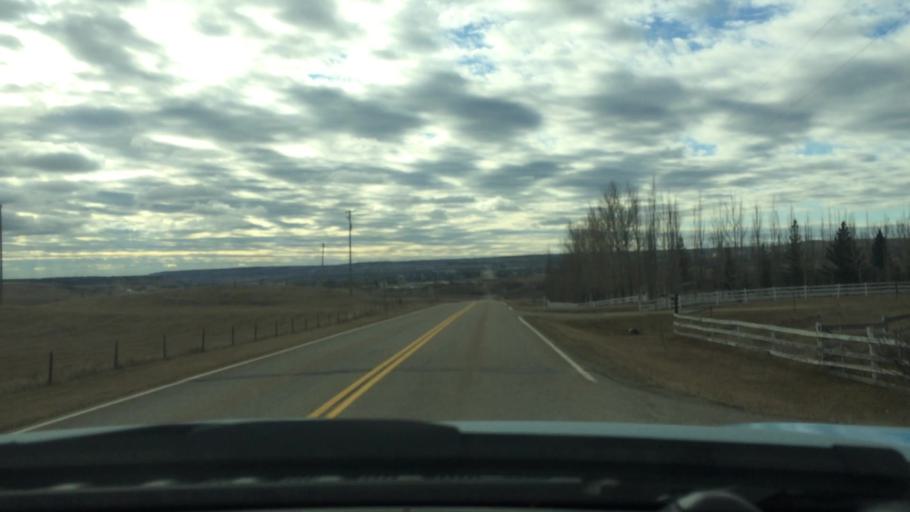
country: CA
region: Alberta
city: Airdrie
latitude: 51.1991
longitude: -114.1412
